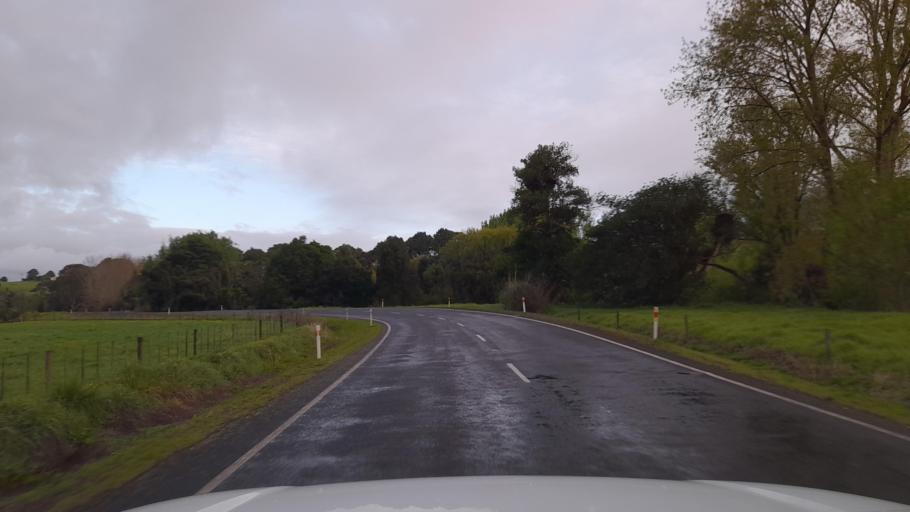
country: NZ
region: Northland
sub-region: Kaipara District
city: Dargaville
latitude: -35.6996
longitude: 173.9132
